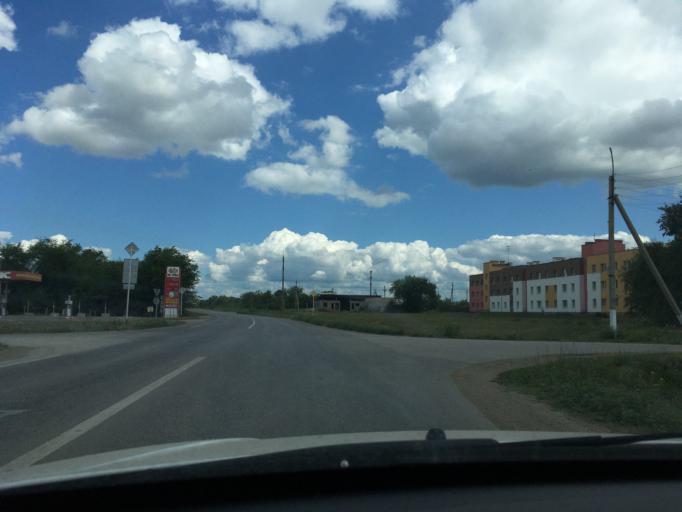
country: RU
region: Samara
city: Bezenchuk
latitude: 52.9954
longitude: 49.4384
